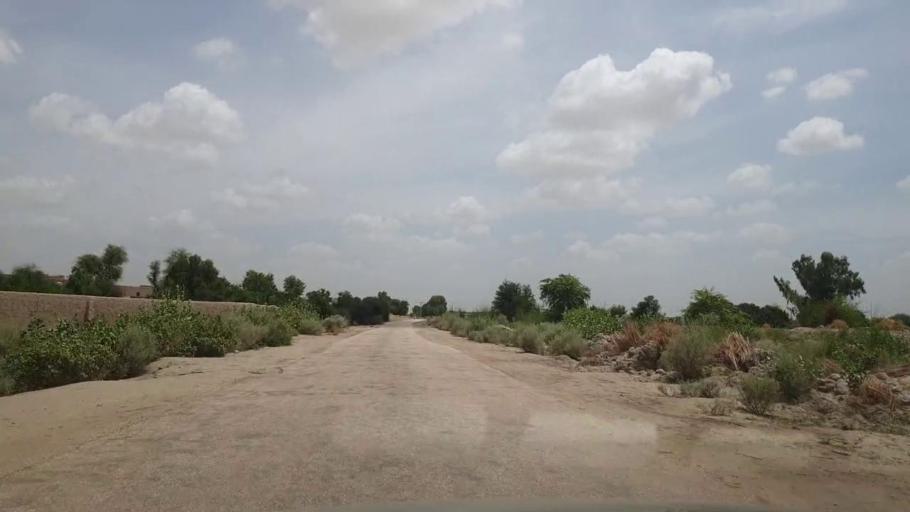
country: PK
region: Sindh
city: Kot Diji
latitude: 27.2097
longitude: 69.1155
